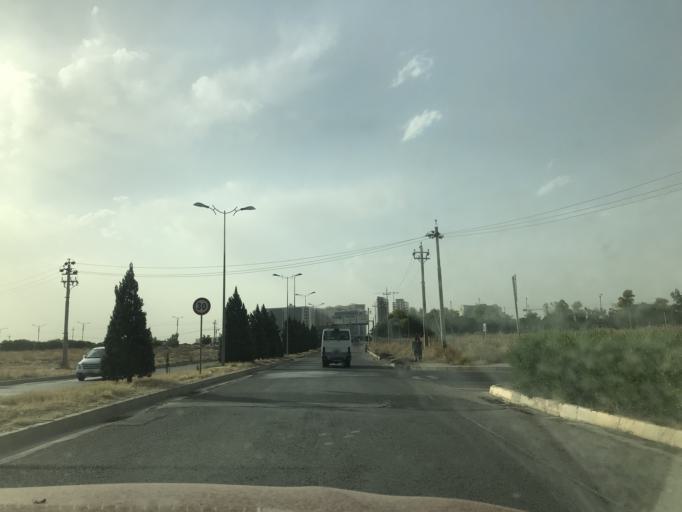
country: IQ
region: Arbil
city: Erbil
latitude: 36.1809
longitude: 43.9763
